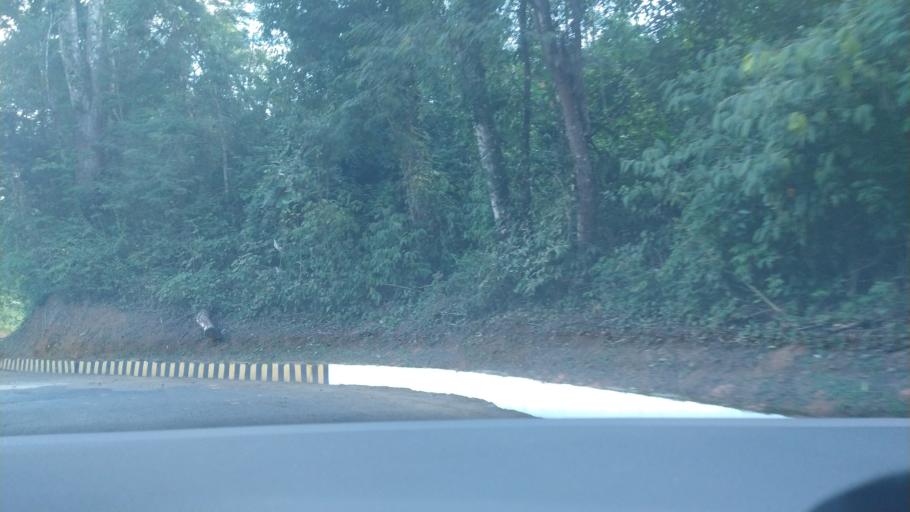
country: BR
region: Minas Gerais
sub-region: Vicosa
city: Vicosa
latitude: -20.7762
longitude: -42.8789
